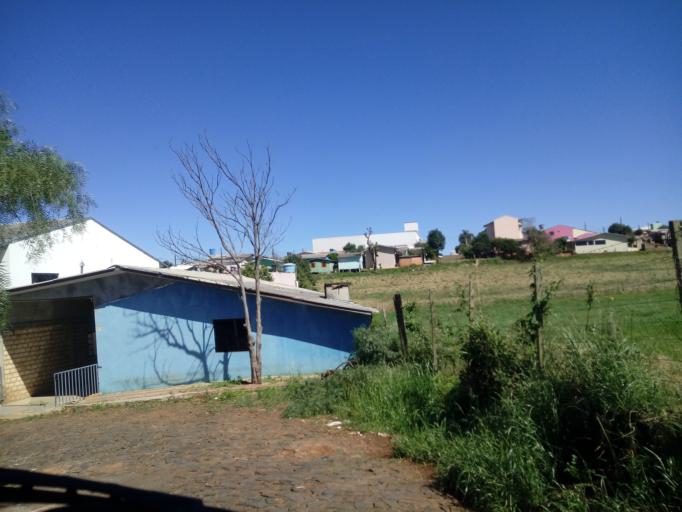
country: BR
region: Santa Catarina
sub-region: Chapeco
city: Chapeco
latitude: -27.0885
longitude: -52.6739
